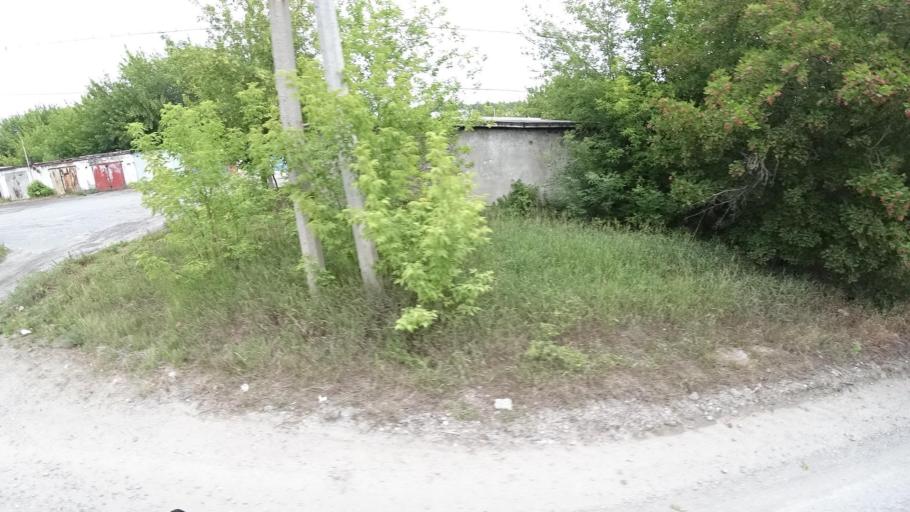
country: RU
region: Sverdlovsk
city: Kamyshlov
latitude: 56.8335
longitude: 62.7199
